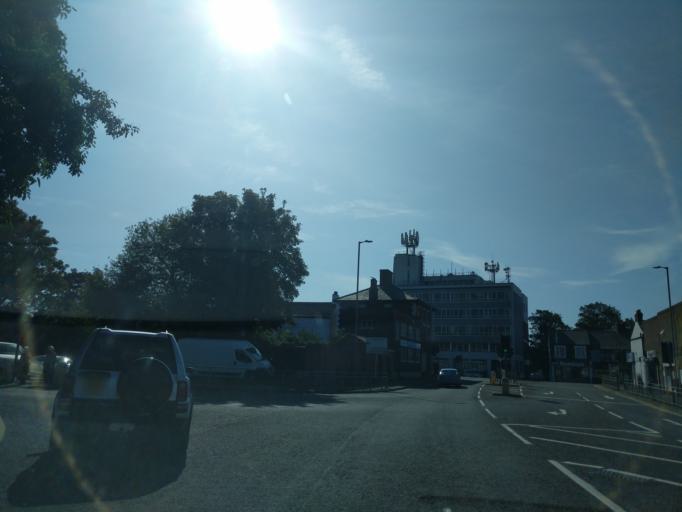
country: GB
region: England
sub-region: Lincolnshire
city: Spalding
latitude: 52.7880
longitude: -0.1564
